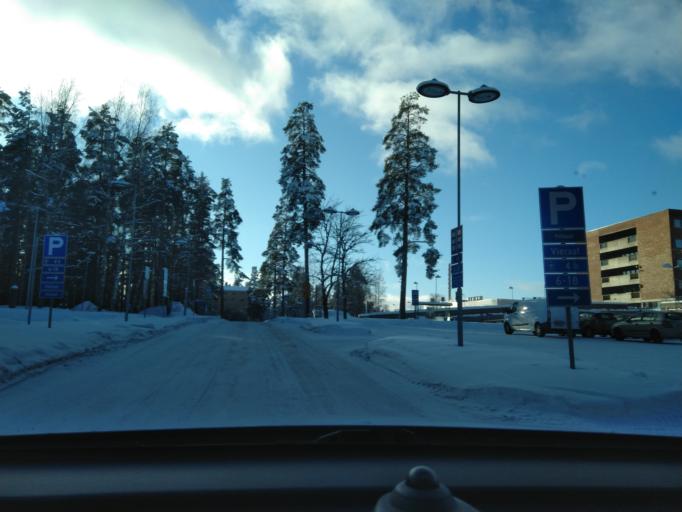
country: FI
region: Haeme
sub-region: Haemeenlinna
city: Haemeenlinna
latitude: 60.9890
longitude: 24.4170
